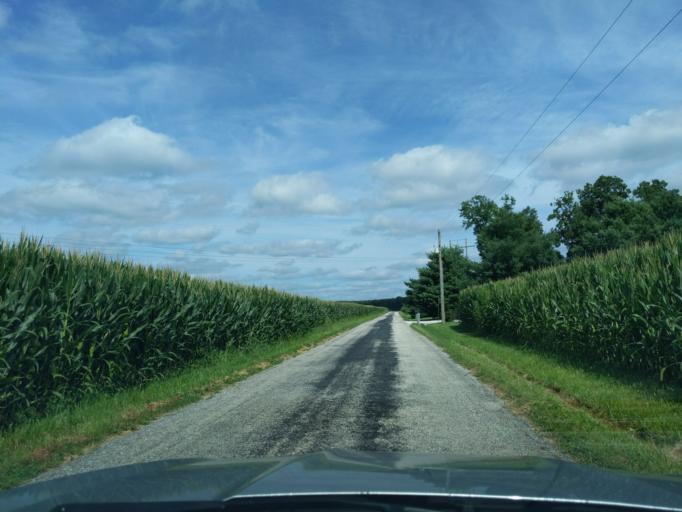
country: US
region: Indiana
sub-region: Ripley County
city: Osgood
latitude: 39.2353
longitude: -85.3709
